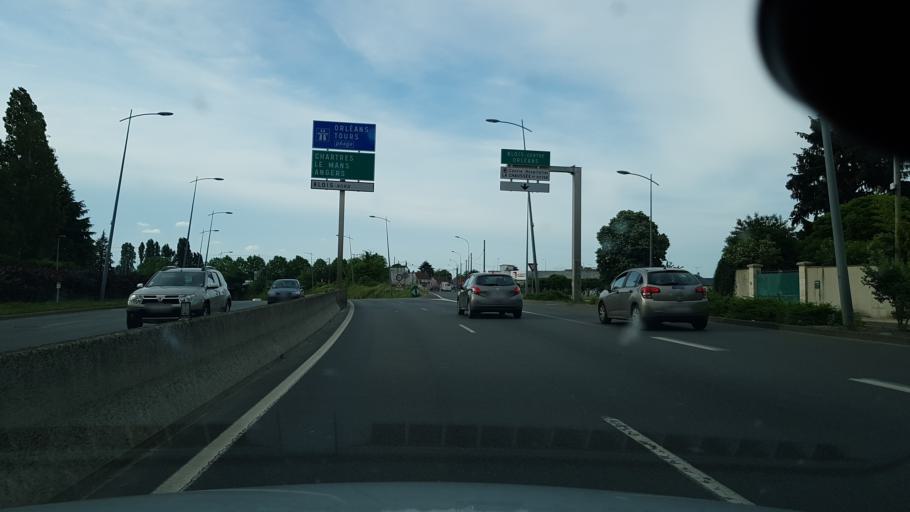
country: FR
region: Centre
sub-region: Departement du Loir-et-Cher
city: Blois
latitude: 47.6002
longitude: 1.3498
